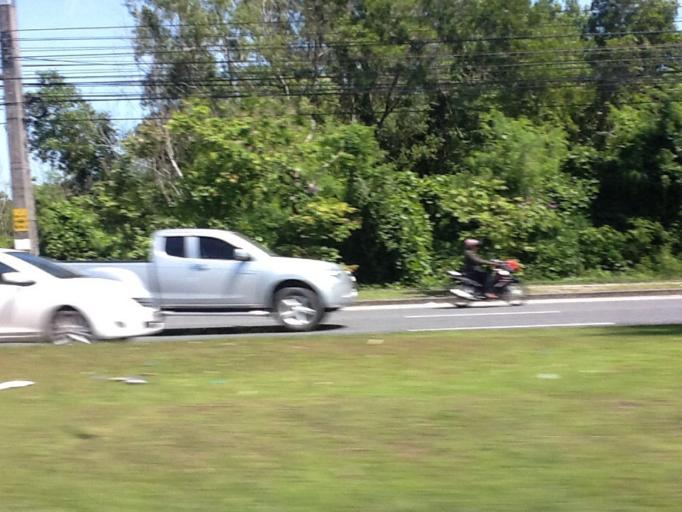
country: TH
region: Phuket
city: Ban Ko Kaeo
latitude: 7.9698
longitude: 98.3702
